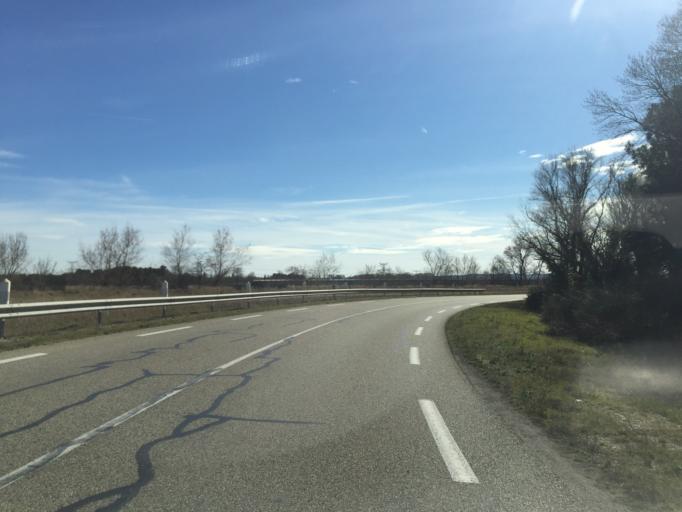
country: FR
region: Languedoc-Roussillon
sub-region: Departement du Gard
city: Laudun-l'Ardoise
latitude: 44.1134
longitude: 4.7087
